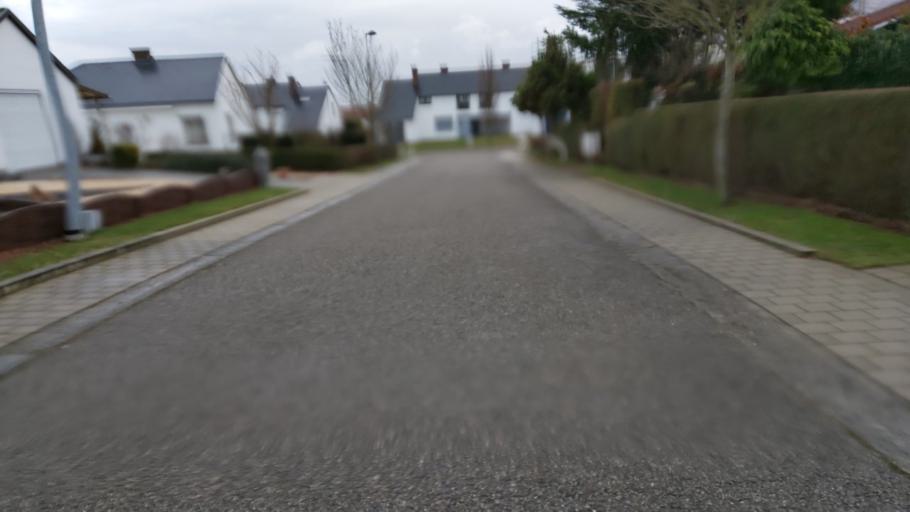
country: BE
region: Flanders
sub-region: Provincie Vlaams-Brabant
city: Tienen
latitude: 50.8166
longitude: 4.9530
